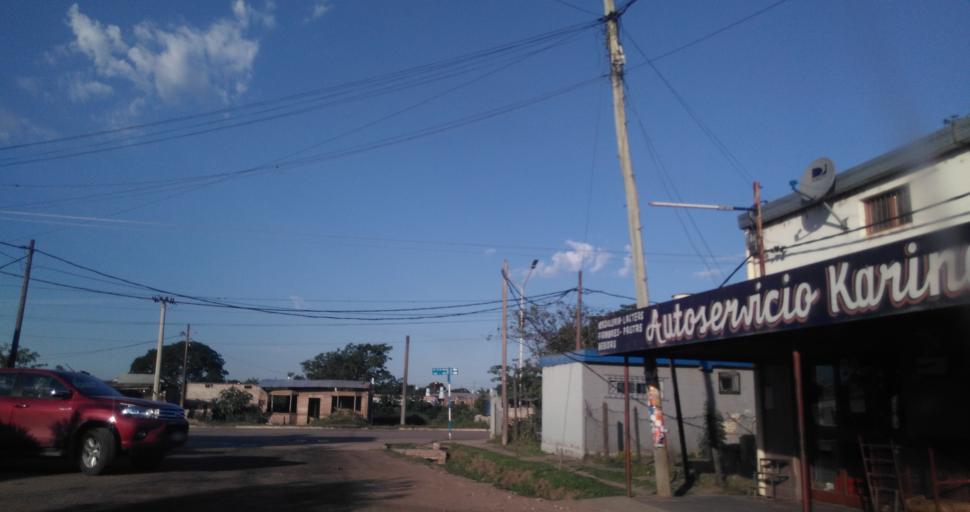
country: AR
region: Chaco
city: Fontana
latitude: -27.4161
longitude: -59.0267
